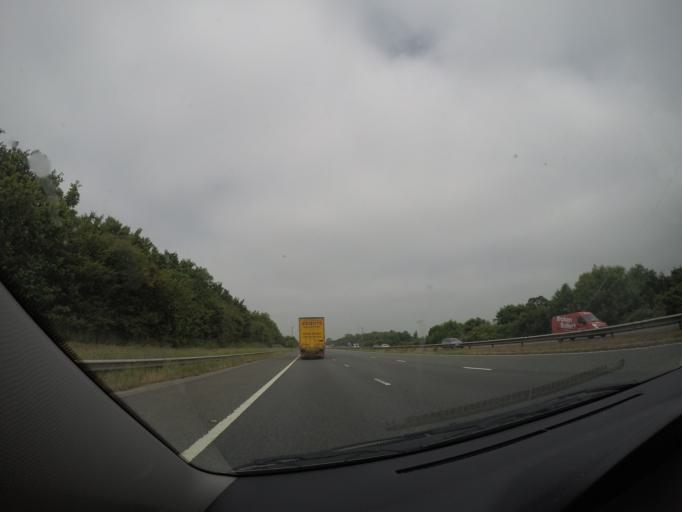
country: GB
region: England
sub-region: North Yorkshire
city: Boroughbridge
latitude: 54.0566
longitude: -1.3896
